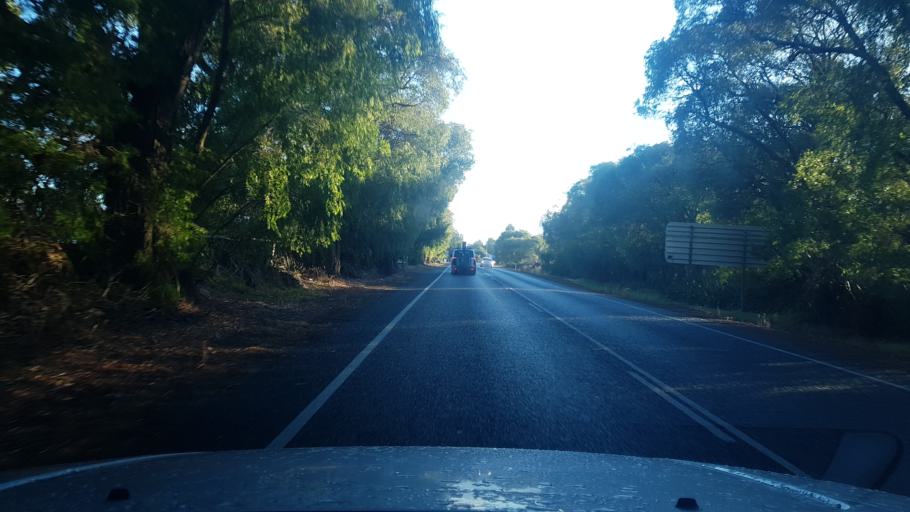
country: AU
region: Western Australia
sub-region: Busselton
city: Vasse
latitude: -33.6655
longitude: 115.2586
